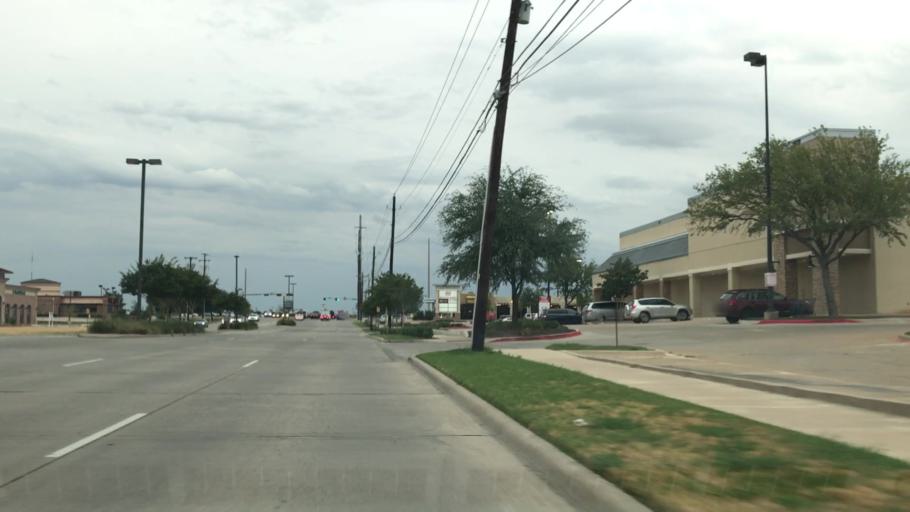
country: US
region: Texas
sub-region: Dallas County
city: Carrollton
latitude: 32.9802
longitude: -96.9098
